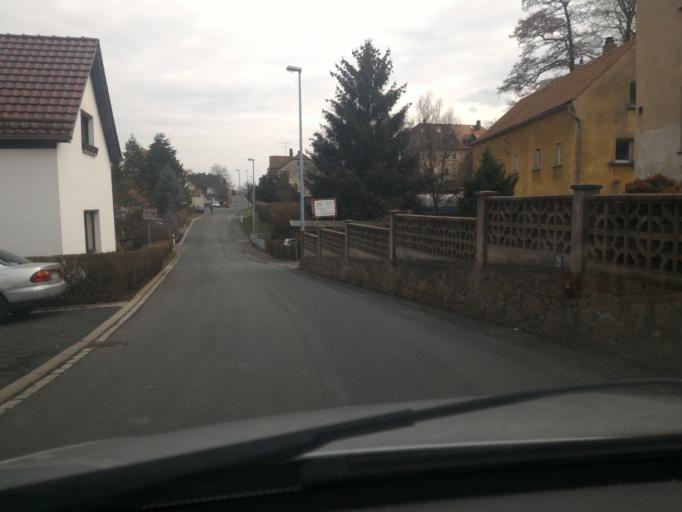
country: DE
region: Saxony
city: Olbersdorf
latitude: 50.8607
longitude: 14.7902
